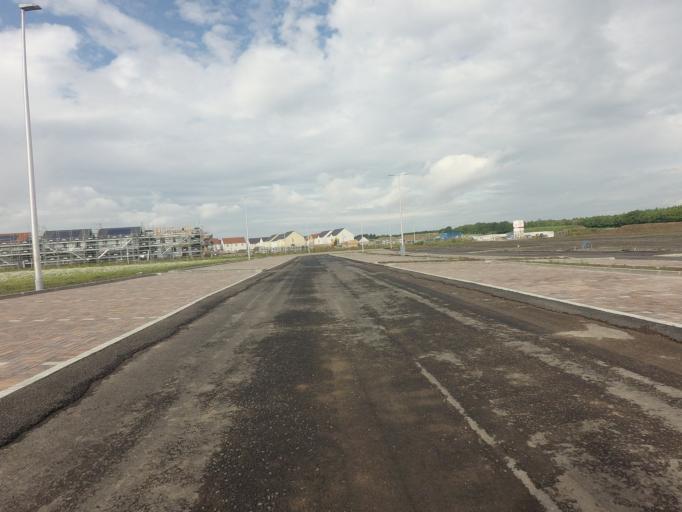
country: GB
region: Scotland
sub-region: West Lothian
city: East Calder
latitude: 55.9042
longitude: -3.4472
